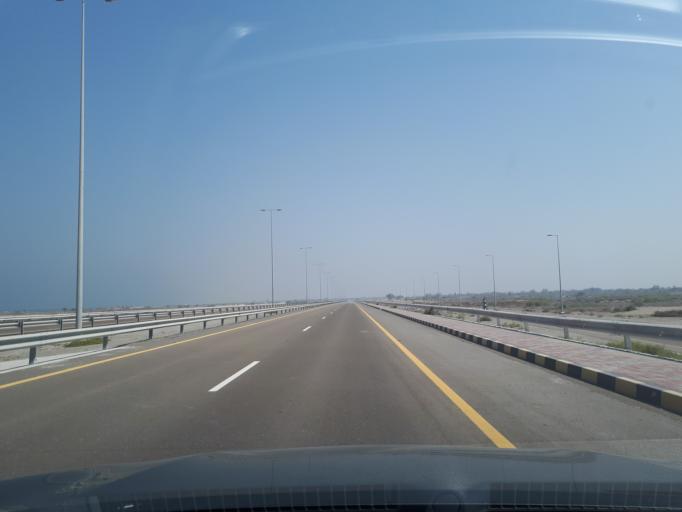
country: AE
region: Al Fujayrah
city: Al Fujayrah
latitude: 24.9390
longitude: 56.3823
